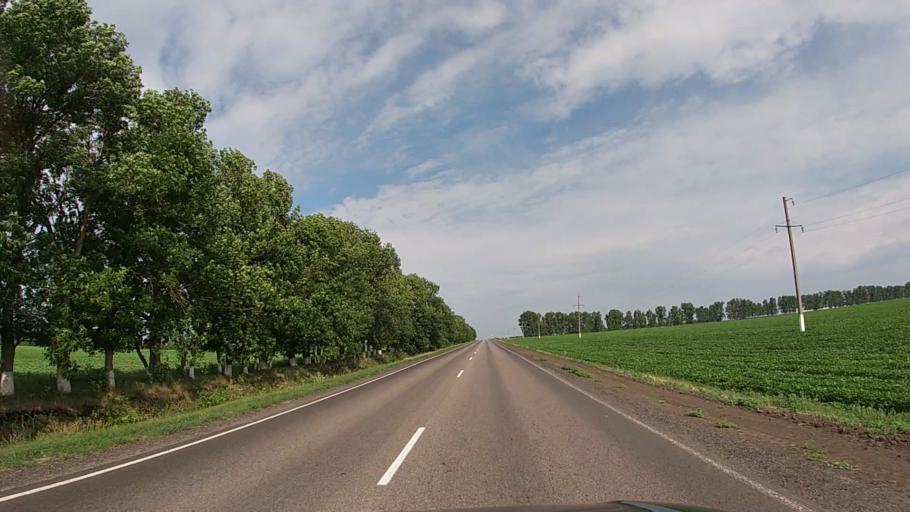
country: RU
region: Belgorod
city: Krasnaya Yaruga
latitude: 50.8040
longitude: 35.5513
